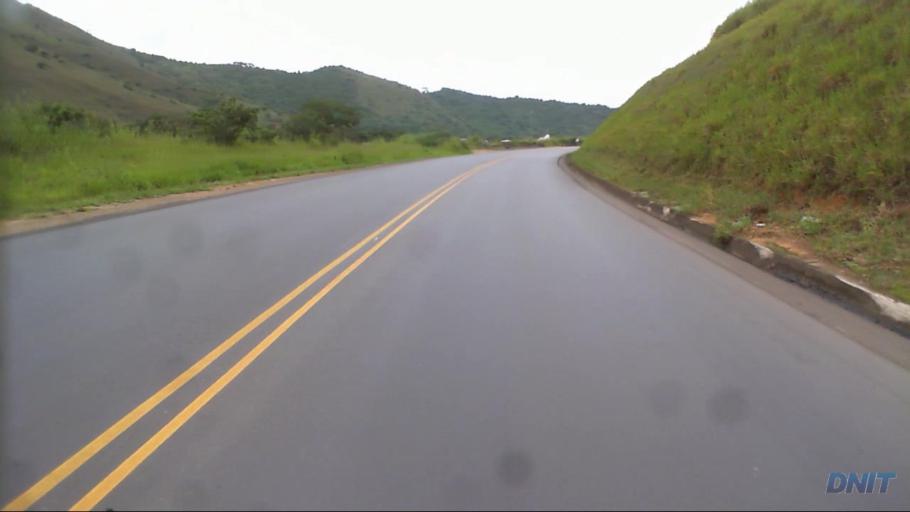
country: BR
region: Minas Gerais
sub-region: Coronel Fabriciano
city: Coronel Fabriciano
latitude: -19.5353
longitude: -42.5909
